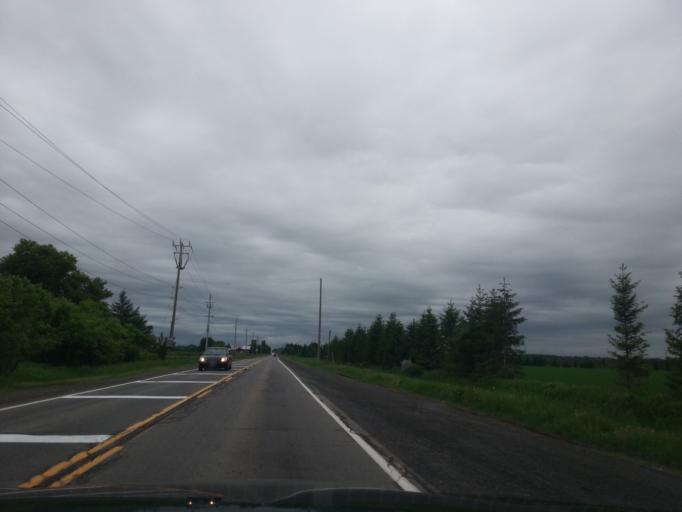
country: CA
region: Ontario
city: Bells Corners
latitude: 45.2371
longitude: -75.8737
